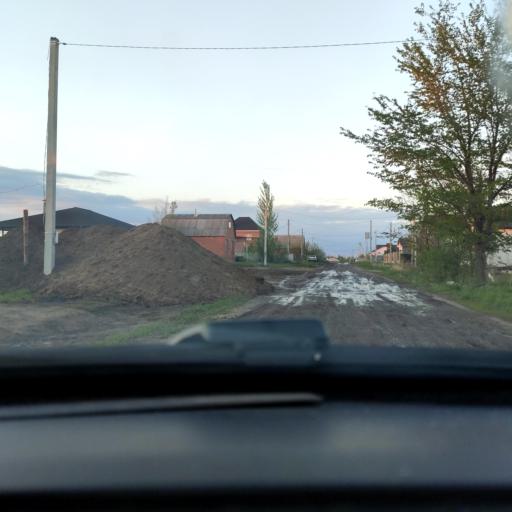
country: RU
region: Voronezj
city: Novaya Usman'
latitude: 51.6561
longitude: 39.4193
